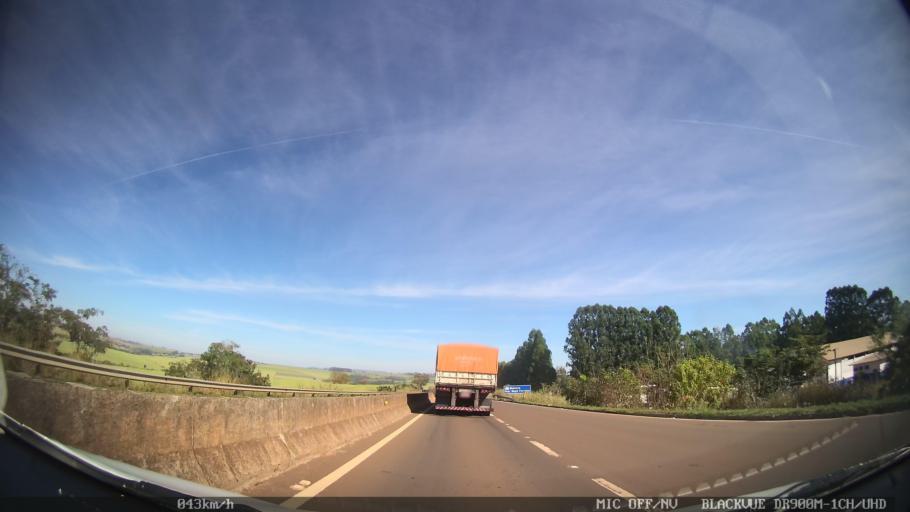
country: BR
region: Sao Paulo
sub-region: Pirassununga
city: Pirassununga
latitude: -22.0392
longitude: -47.4340
